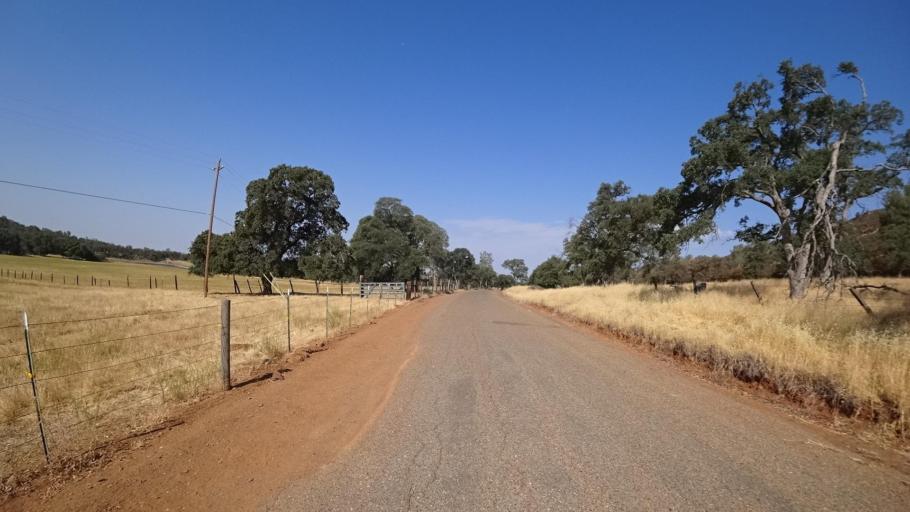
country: US
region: California
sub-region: Tuolumne County
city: Tuolumne City
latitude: 37.7225
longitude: -120.2862
